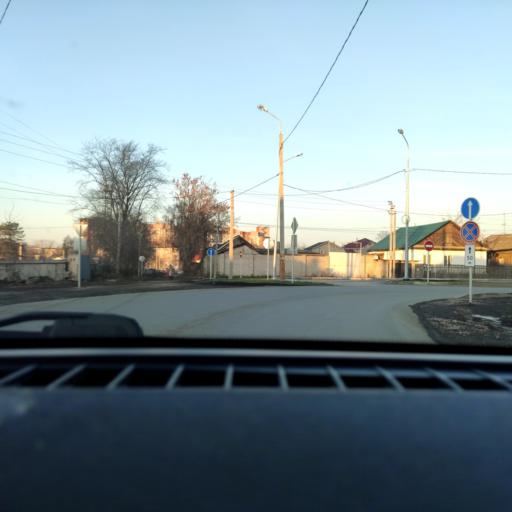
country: RU
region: Perm
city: Perm
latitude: 57.9752
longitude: 56.1948
